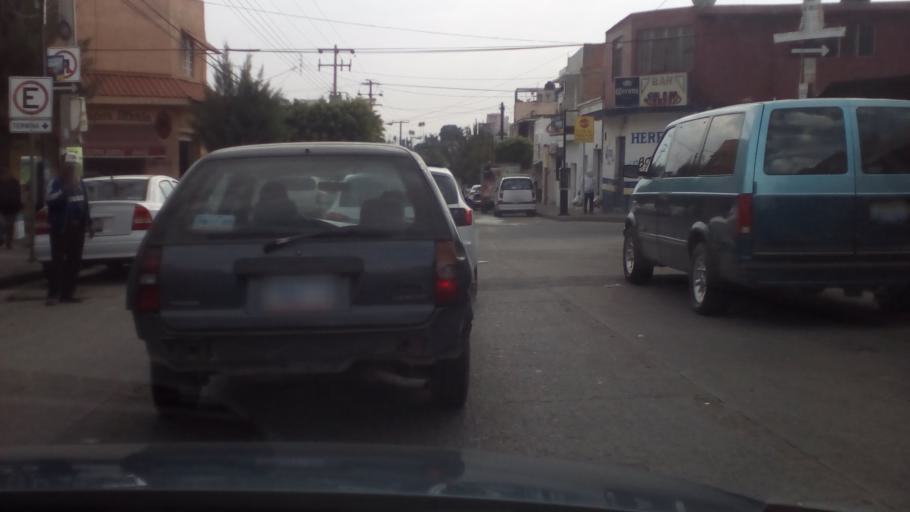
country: MX
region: Guanajuato
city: Leon
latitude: 21.1309
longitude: -101.6962
